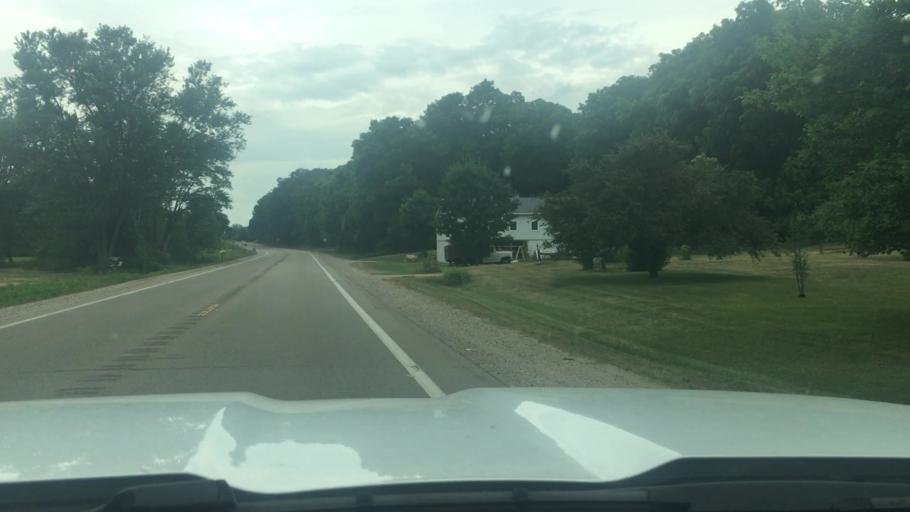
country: US
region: Michigan
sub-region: Ionia County
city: Saranac
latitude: 42.9340
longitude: -85.2634
